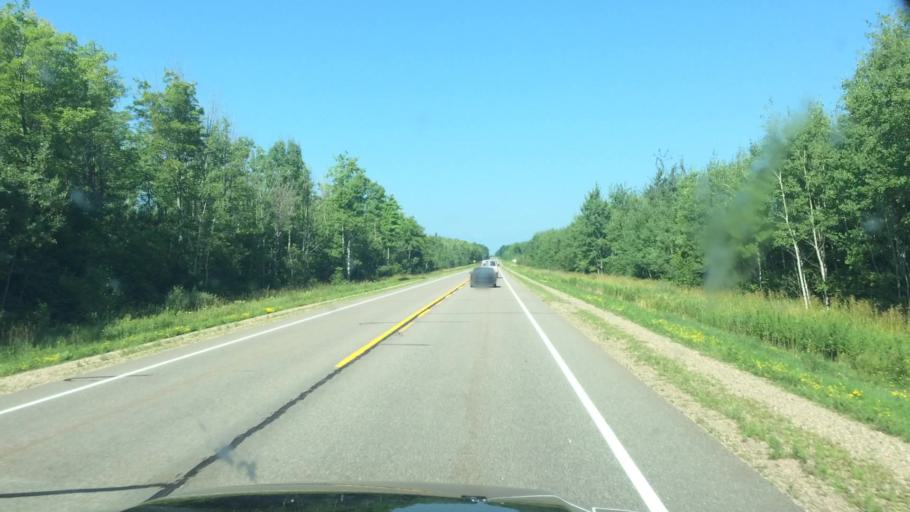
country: US
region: Wisconsin
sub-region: Langlade County
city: Antigo
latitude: 45.1469
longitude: -89.3654
